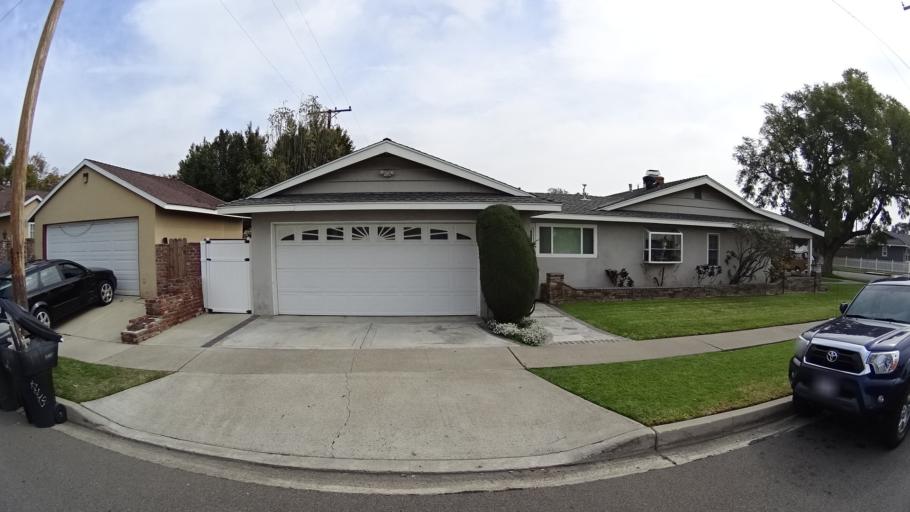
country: US
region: California
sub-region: Orange County
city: Anaheim
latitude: 33.8206
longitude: -117.9502
